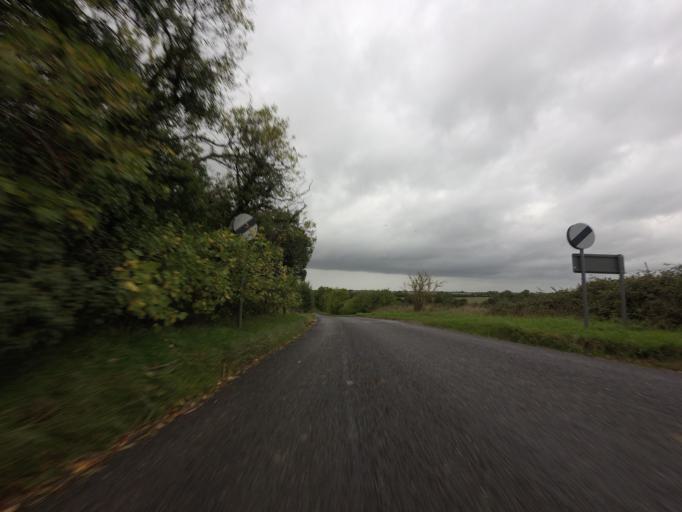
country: GB
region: England
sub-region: Cambridgeshire
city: Wimpole
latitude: 52.1798
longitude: -0.0376
